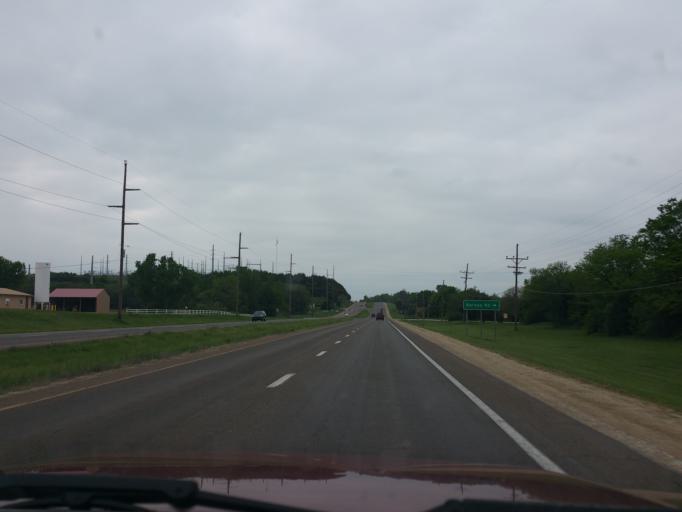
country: US
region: Kansas
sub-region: Riley County
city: Manhattan
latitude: 39.2273
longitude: -96.5833
